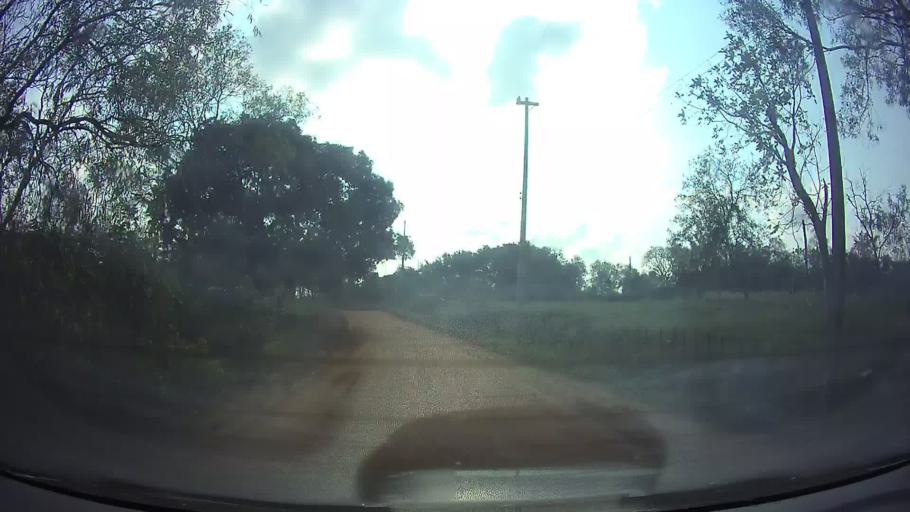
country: PY
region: Cordillera
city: Arroyos y Esteros
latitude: -25.0523
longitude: -57.1773
